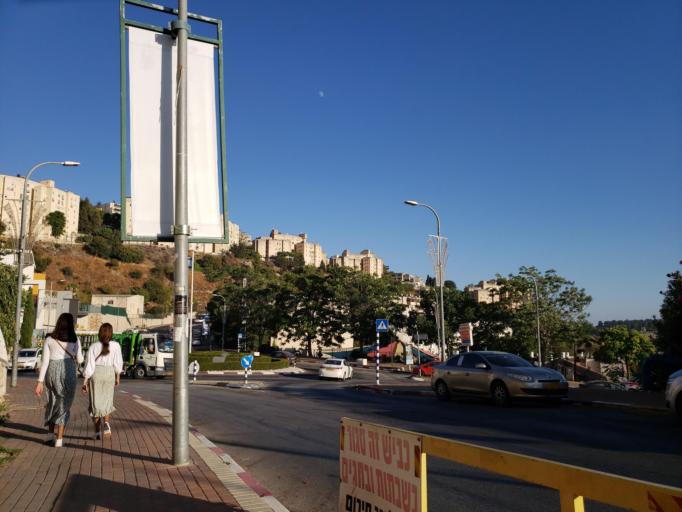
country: IL
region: Northern District
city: Safed
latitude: 32.9642
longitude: 35.4886
